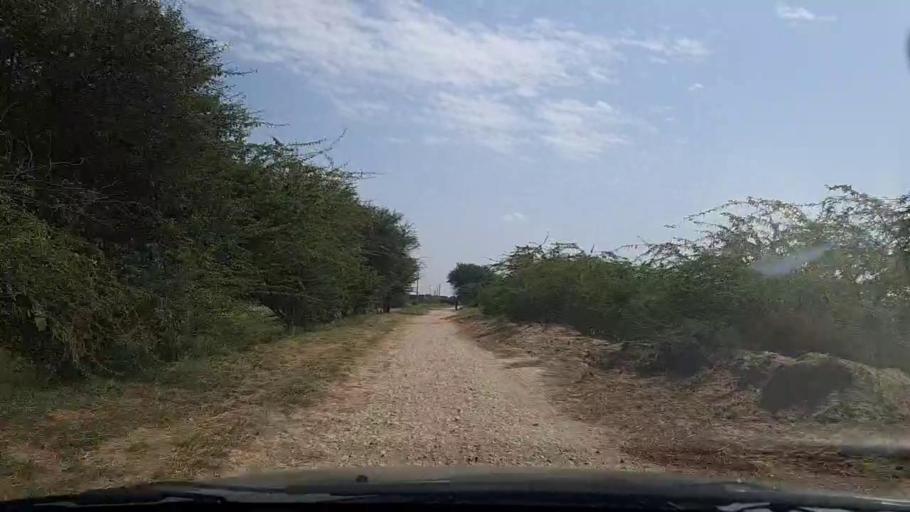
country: PK
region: Sindh
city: Mirpur Batoro
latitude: 24.5706
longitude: 68.1975
